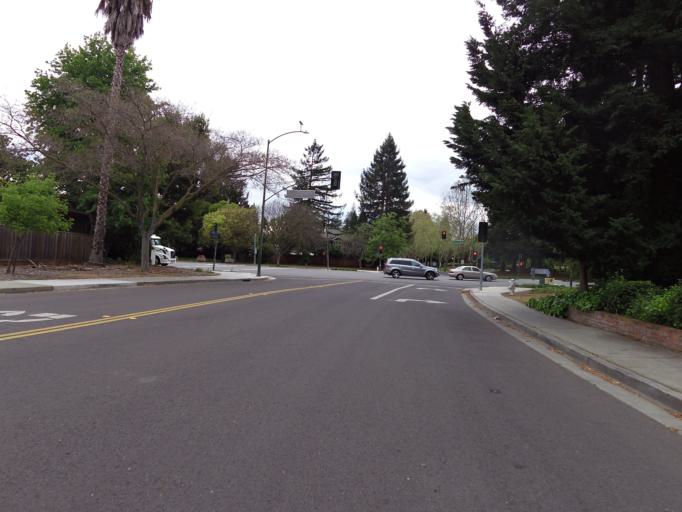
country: US
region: California
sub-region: Santa Clara County
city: Mountain View
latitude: 37.3907
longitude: -122.0871
